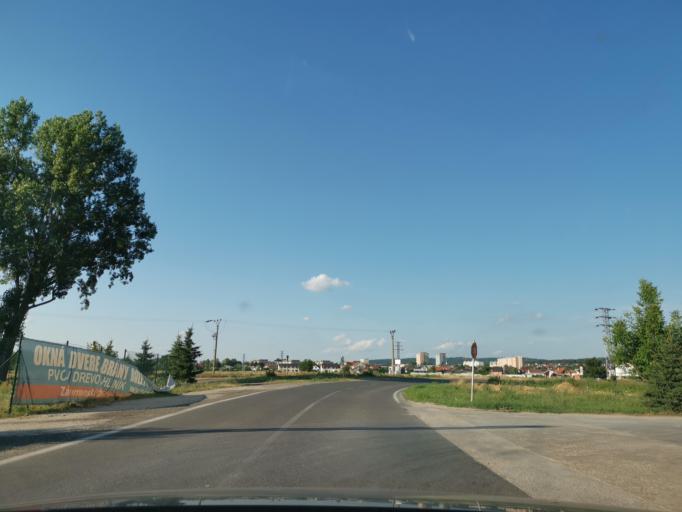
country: SK
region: Bratislavsky
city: Stupava
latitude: 48.2620
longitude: 17.0209
